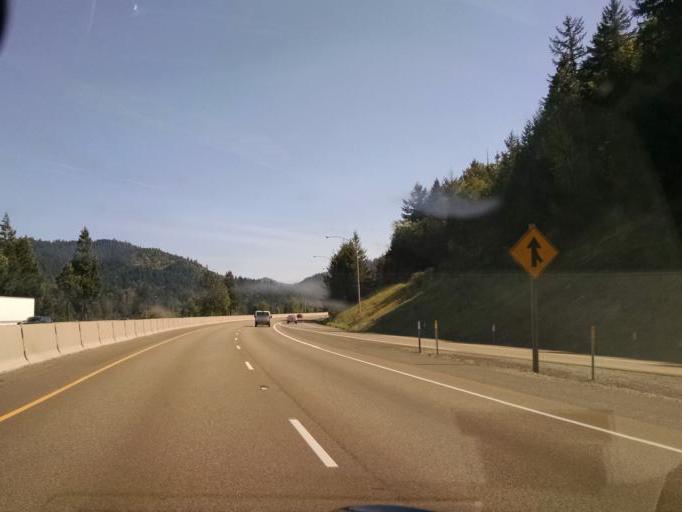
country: US
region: Oregon
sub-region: Douglas County
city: Canyonville
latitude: 42.9398
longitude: -123.2871
